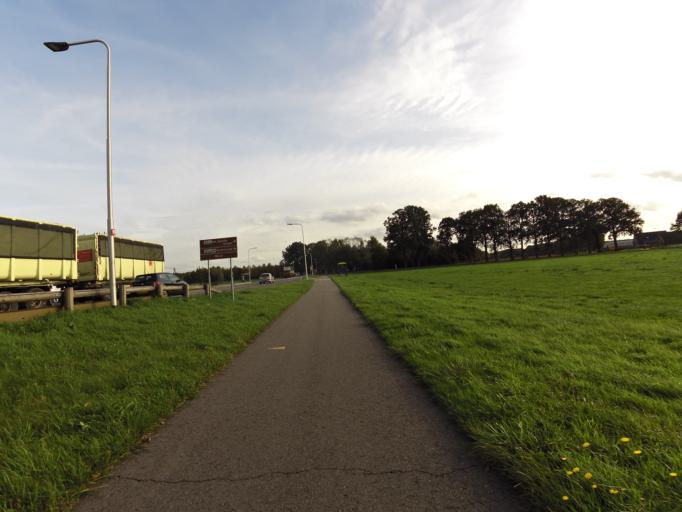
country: NL
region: Gelderland
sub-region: Gemeente Bronckhorst
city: Baak
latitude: 52.0307
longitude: 6.2137
